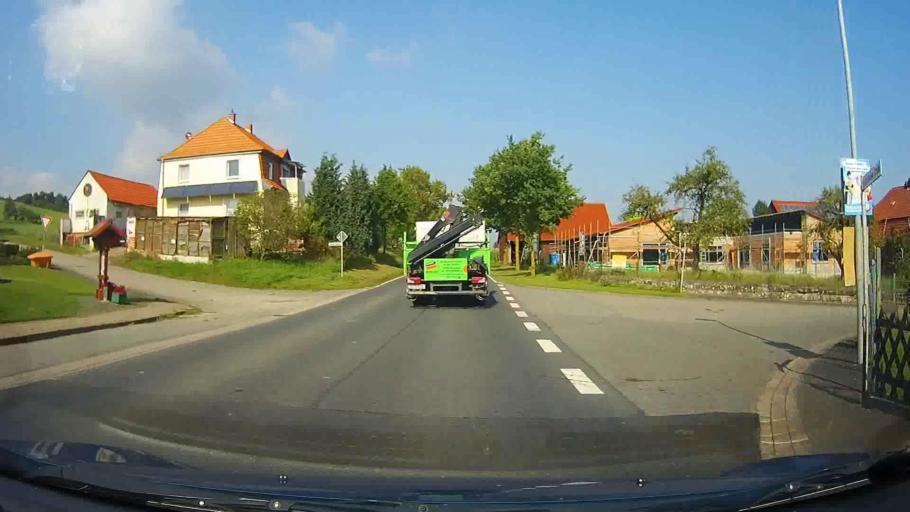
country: DE
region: Lower Saxony
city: Hardegsen
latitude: 51.6641
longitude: 9.8464
